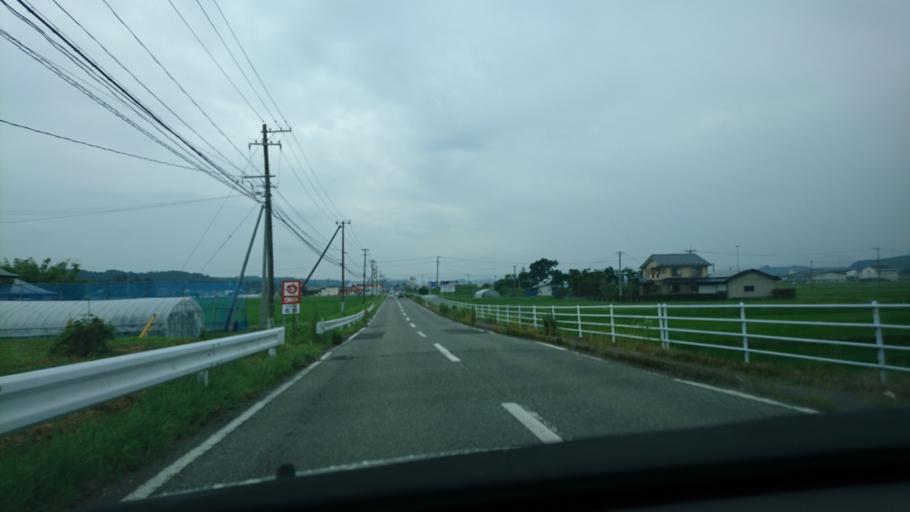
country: JP
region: Miyagi
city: Furukawa
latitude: 38.7332
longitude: 140.9643
